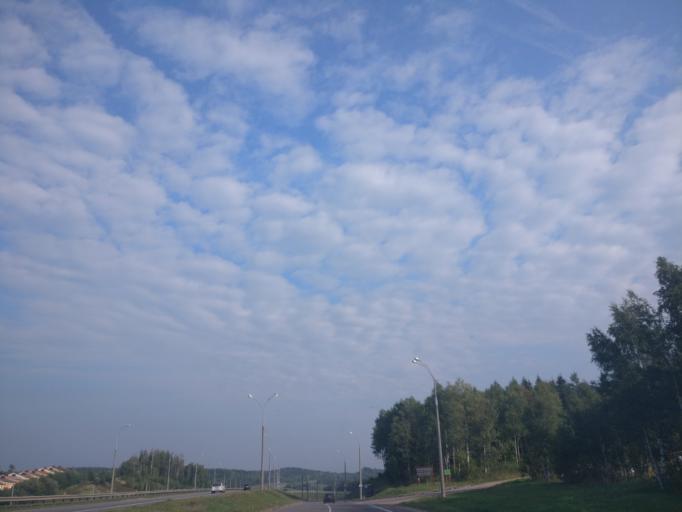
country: BY
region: Minsk
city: Lahoysk
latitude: 54.1754
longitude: 27.8198
